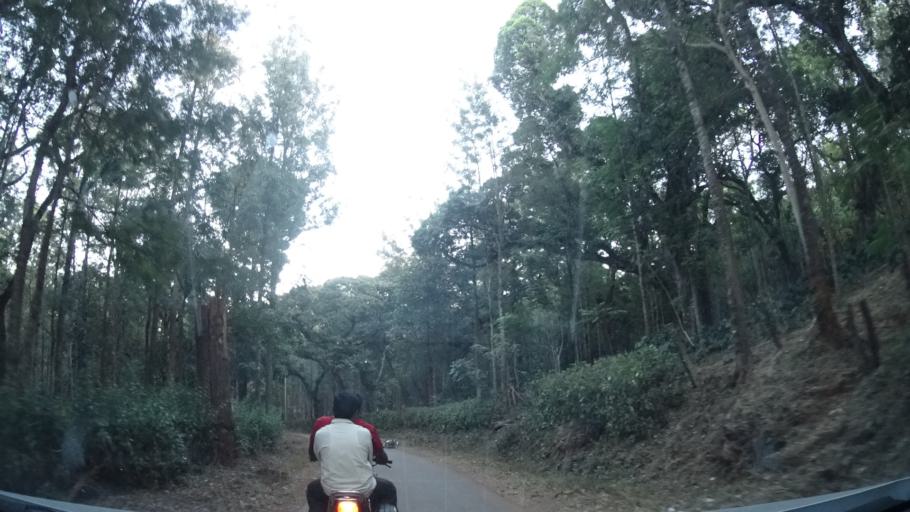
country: IN
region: Karnataka
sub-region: Chikmagalur
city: Tarikere
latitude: 13.5646
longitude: 75.7670
